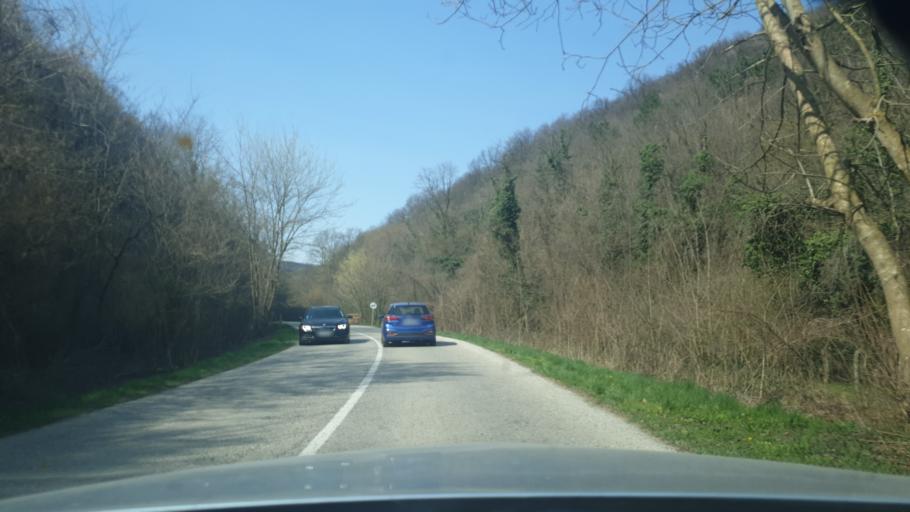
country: RS
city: Vrdnik
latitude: 45.1405
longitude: 19.7738
